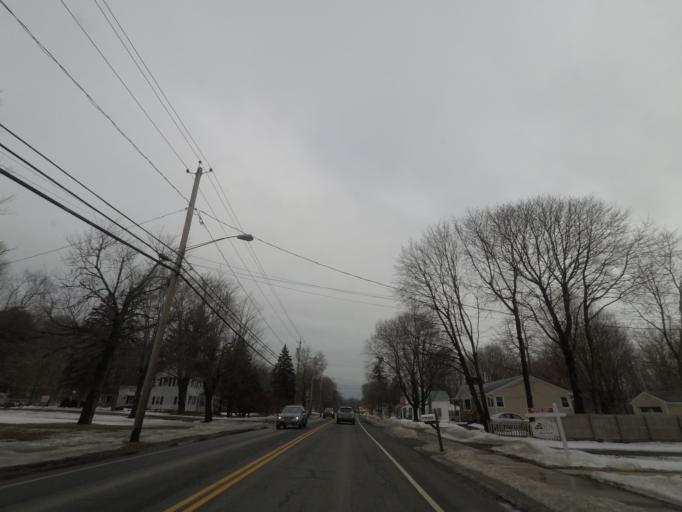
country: US
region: New York
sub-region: Albany County
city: Voorheesville
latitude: 42.7038
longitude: -73.9689
